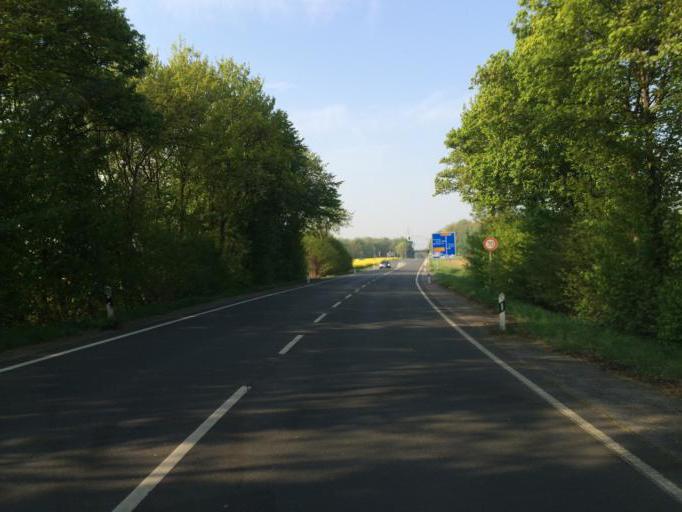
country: DE
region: North Rhine-Westphalia
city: Witten
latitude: 51.4634
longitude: 7.3901
